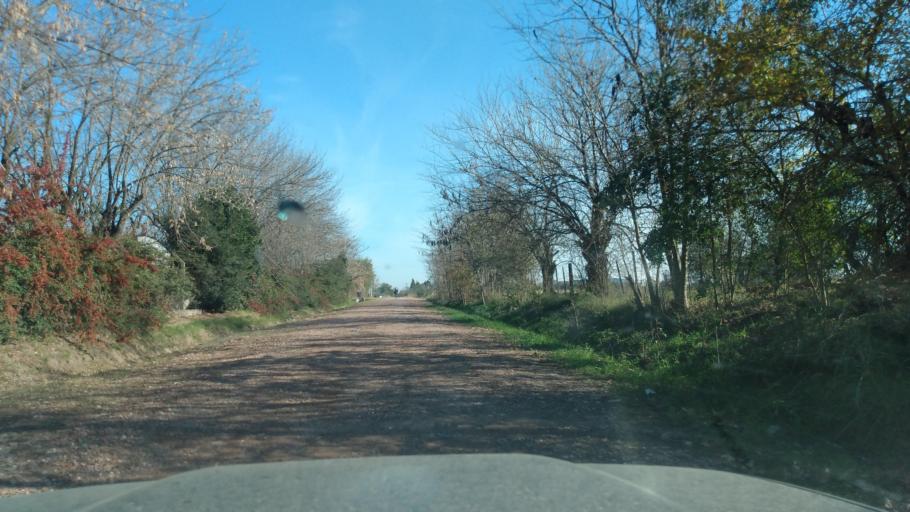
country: AR
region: Buenos Aires
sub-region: Partido de Lujan
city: Lujan
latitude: -34.5644
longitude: -59.1362
